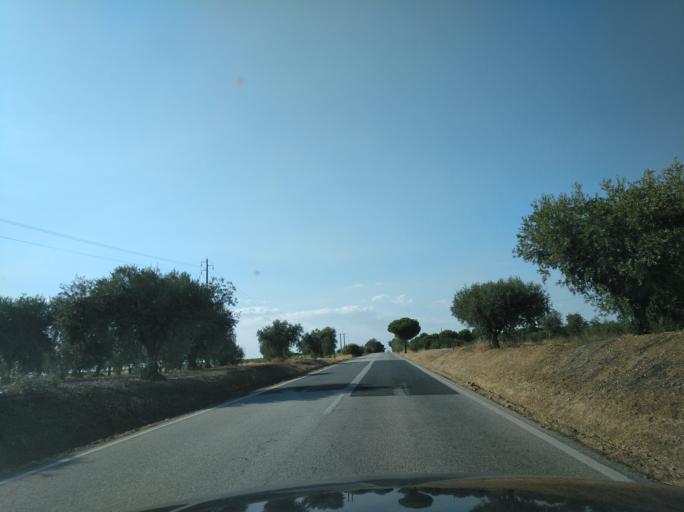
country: ES
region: Extremadura
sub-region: Provincia de Badajoz
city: Valencia del Mombuey
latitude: 38.2312
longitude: -7.2333
